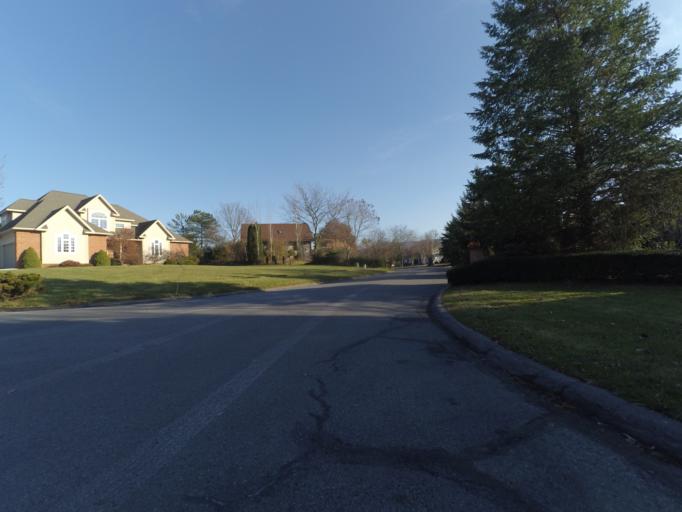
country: US
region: Pennsylvania
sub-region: Centre County
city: Lemont
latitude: 40.7937
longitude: -77.8289
